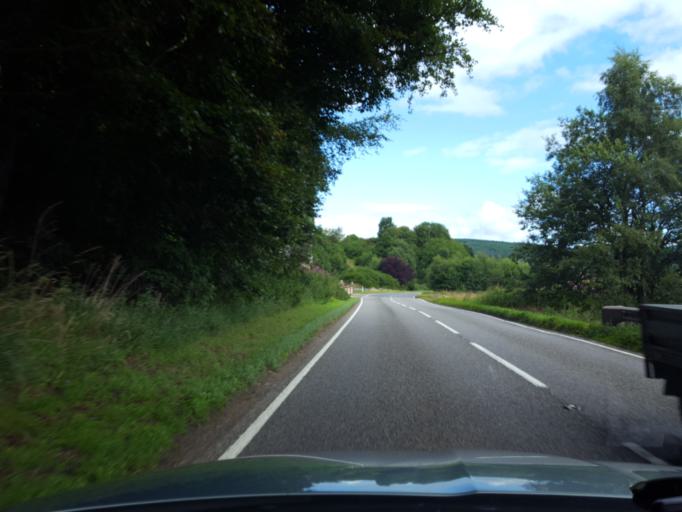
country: GB
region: Scotland
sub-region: Moray
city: Rothes
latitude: 57.5189
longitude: -3.2093
